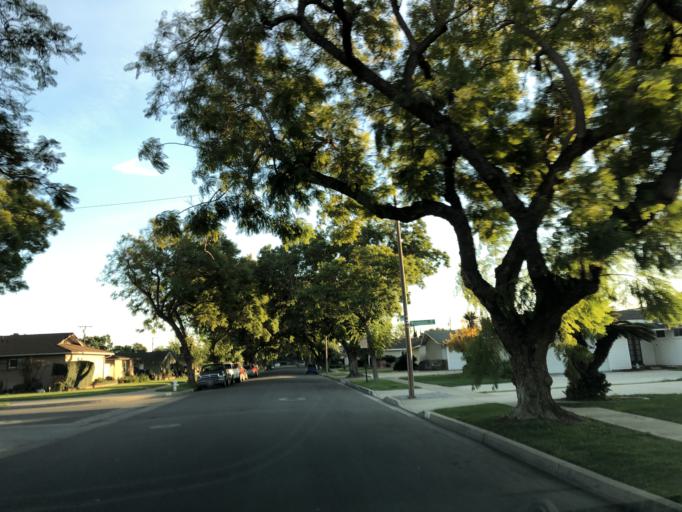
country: US
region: California
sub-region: Orange County
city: Santa Ana
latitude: 33.7568
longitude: -117.8488
